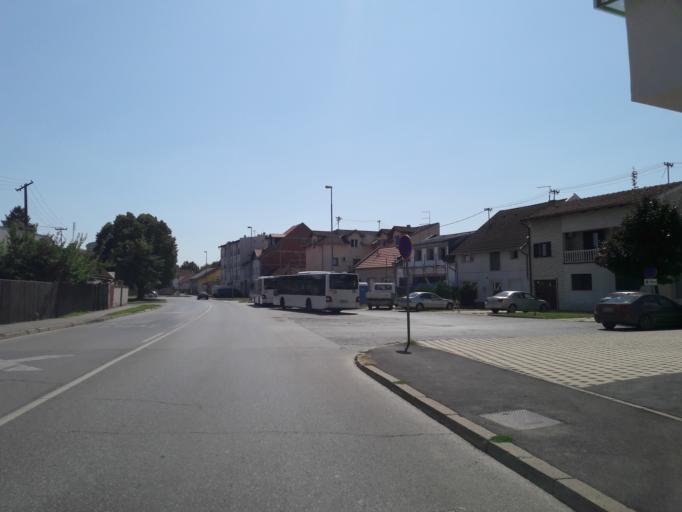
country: HR
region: Osjecko-Baranjska
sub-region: Grad Osijek
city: Osijek
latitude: 45.5605
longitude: 18.6616
